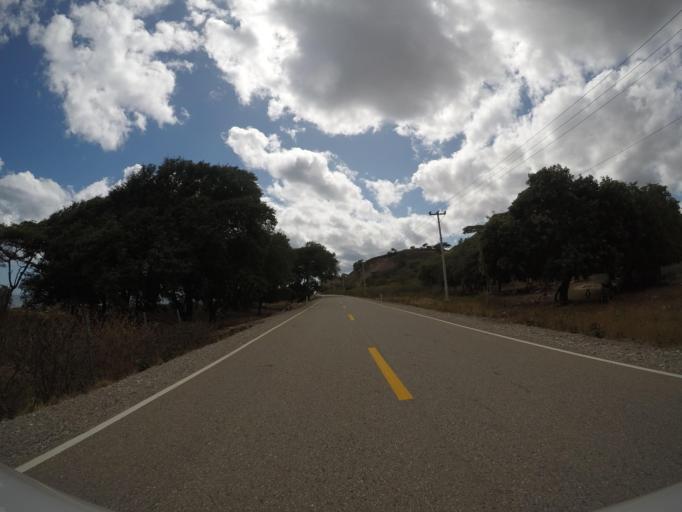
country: TL
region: Lautem
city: Lospalos
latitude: -8.4064
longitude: 126.8136
